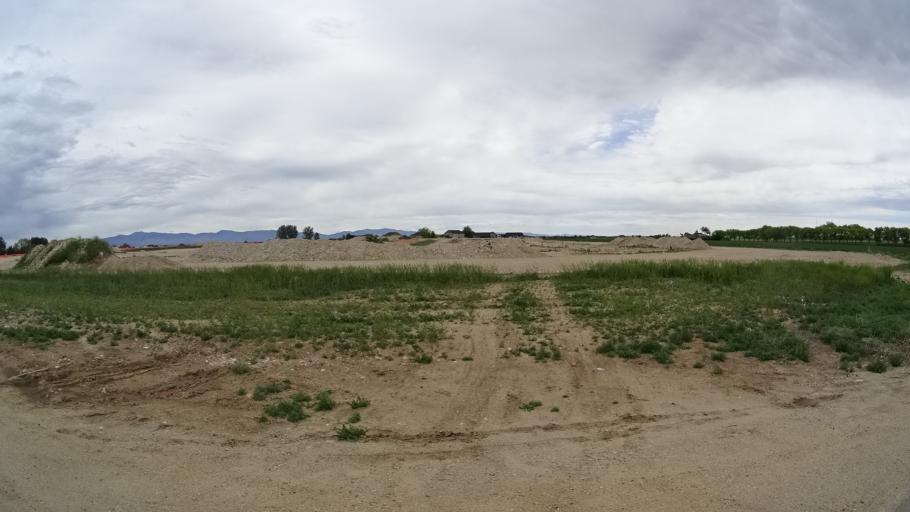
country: US
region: Idaho
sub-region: Ada County
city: Meridian
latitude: 43.5726
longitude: -116.4139
